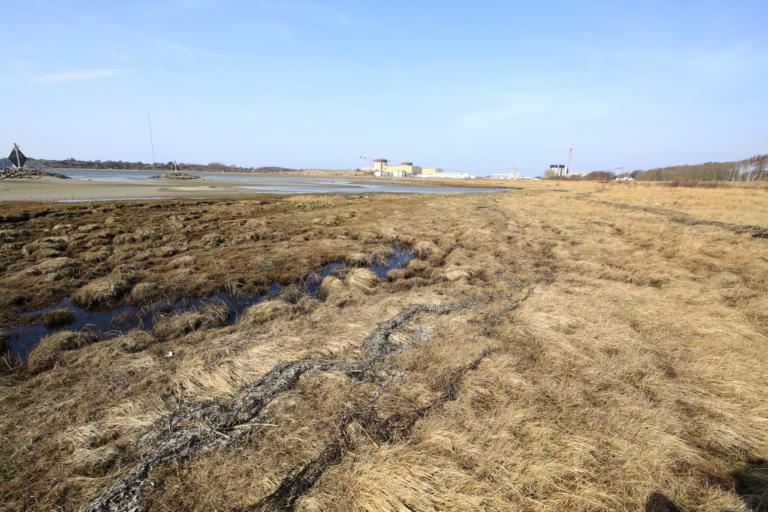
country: SE
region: Halland
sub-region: Kungsbacka Kommun
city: Frillesas
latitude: 57.2525
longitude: 12.1234
